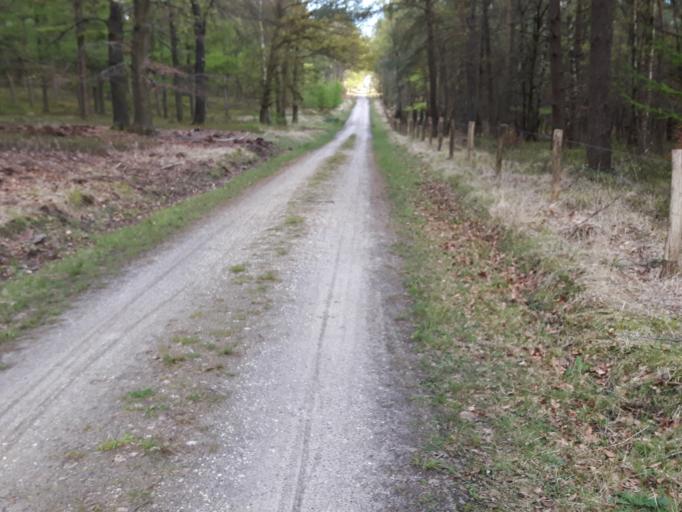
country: NL
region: Gelderland
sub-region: Gemeente Apeldoorn
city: Loenen
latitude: 52.0816
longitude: 5.9625
